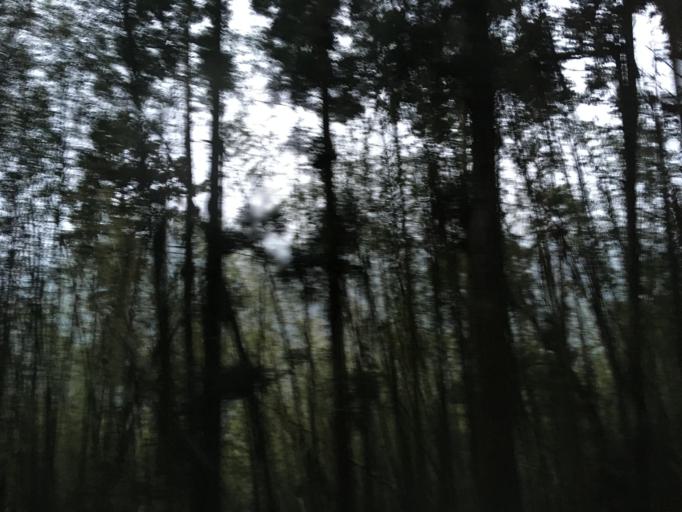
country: TW
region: Taiwan
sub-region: Chiayi
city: Jiayi Shi
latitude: 23.5117
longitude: 120.6588
